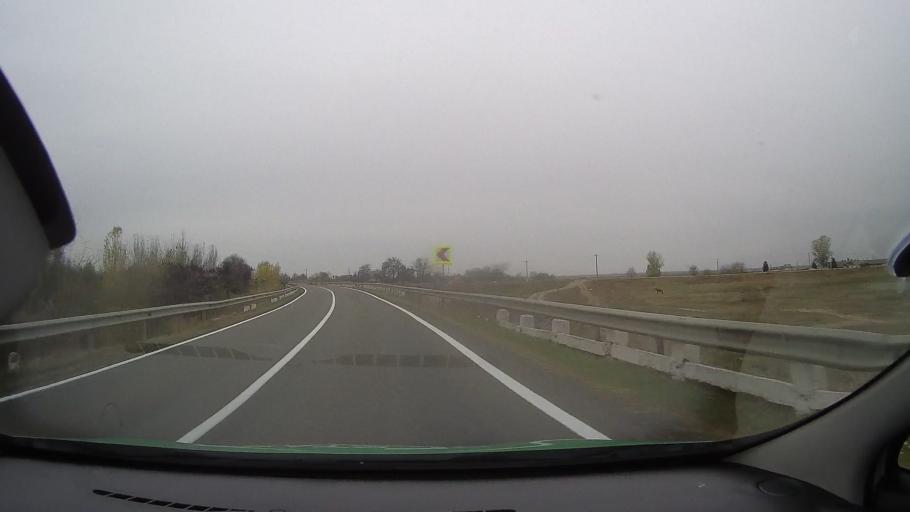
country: RO
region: Ialomita
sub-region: Comuna Giurgeni
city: Giurgeni
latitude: 44.7544
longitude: 27.8588
